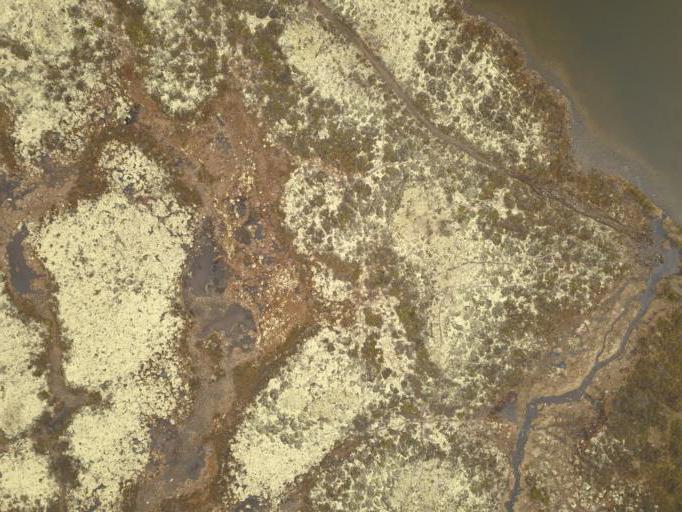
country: NO
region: Hedmark
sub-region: Folldal
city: Folldal
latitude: 62.2298
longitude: 9.6486
